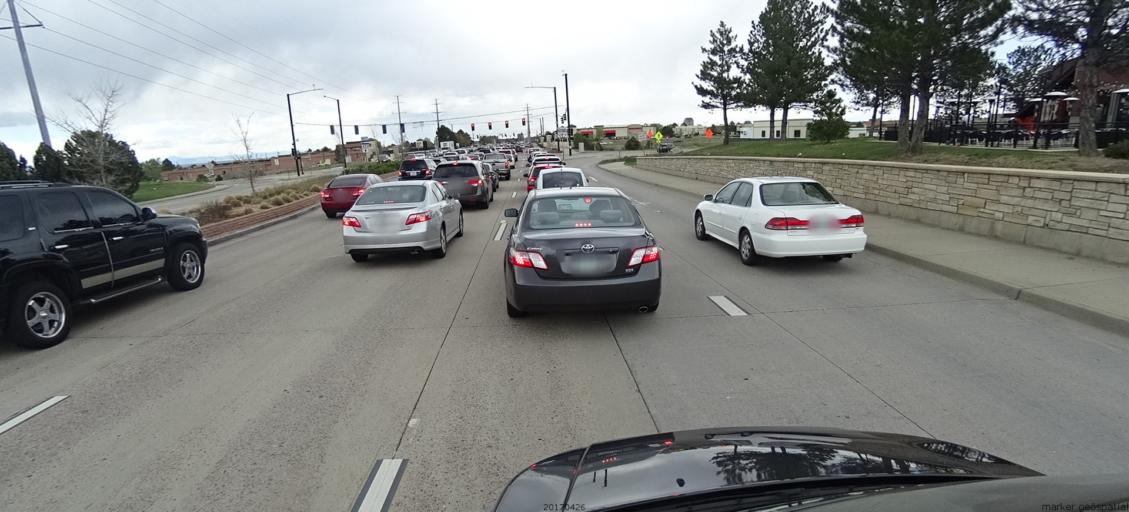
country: US
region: Colorado
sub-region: Douglas County
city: Acres Green
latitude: 39.5622
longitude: -104.9043
